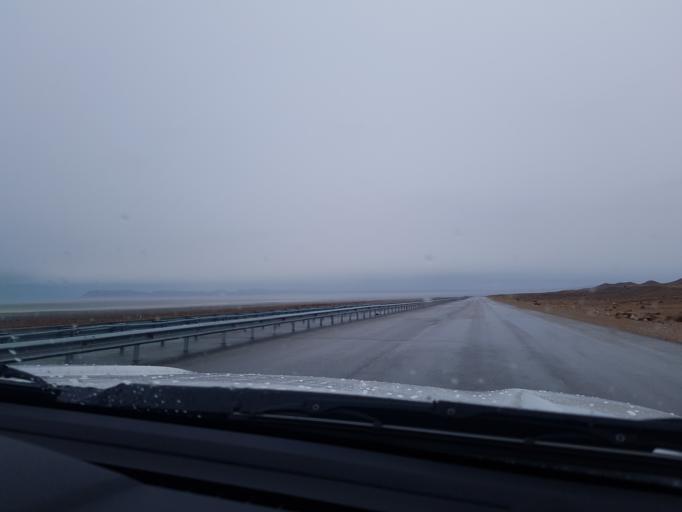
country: TM
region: Balkan
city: Turkmenbasy
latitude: 40.0339
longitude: 53.4812
